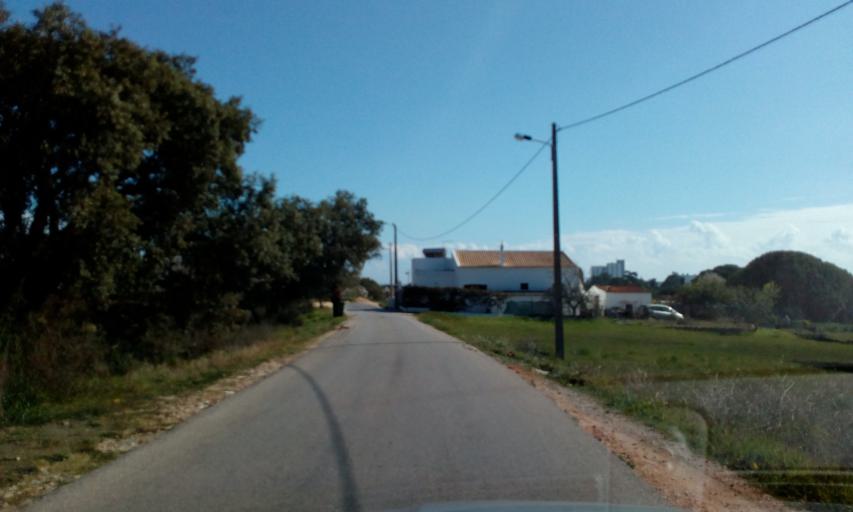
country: PT
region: Faro
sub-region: Albufeira
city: Ferreiras
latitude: 37.0966
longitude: -8.2041
